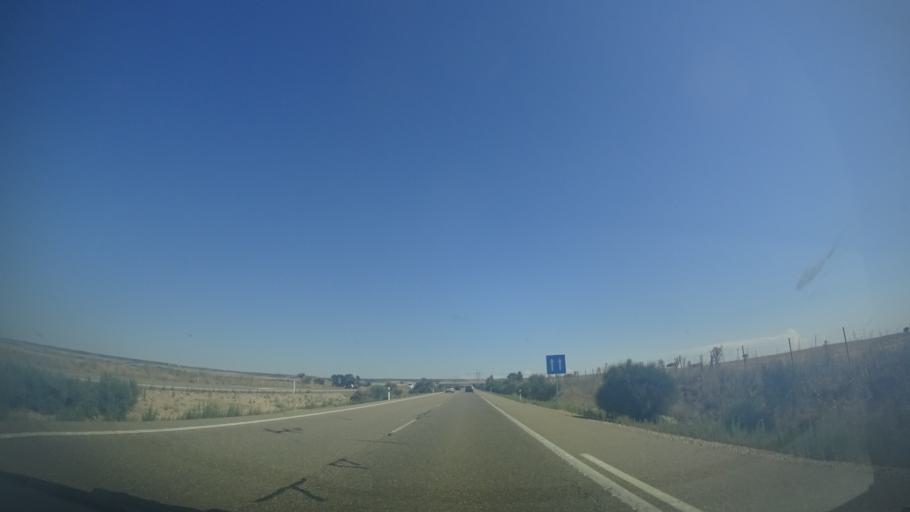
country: ES
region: Castille and Leon
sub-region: Provincia de Valladolid
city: San Pedro de Latarce
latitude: 41.7639
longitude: -5.2979
